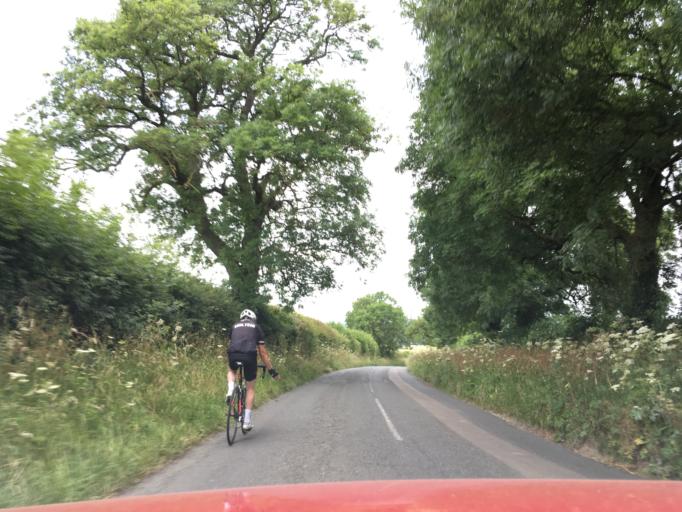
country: GB
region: England
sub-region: Oxfordshire
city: Shipton under Wychwood
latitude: 51.8800
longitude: -1.6574
